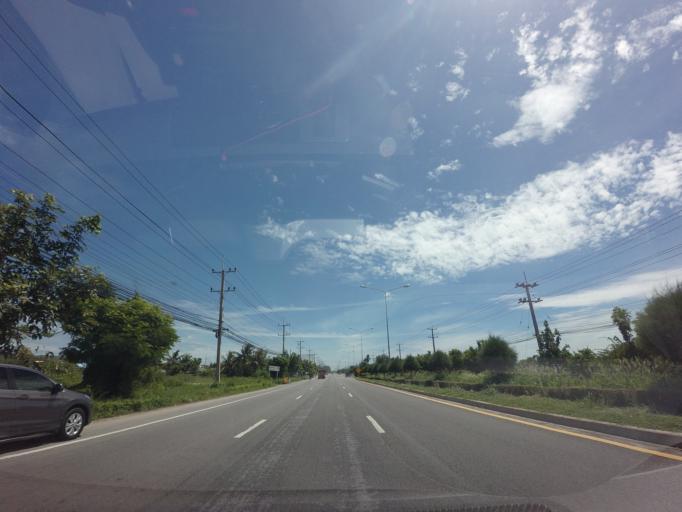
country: TH
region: Phetchaburi
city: Cha-am
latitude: 12.6963
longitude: 99.9530
